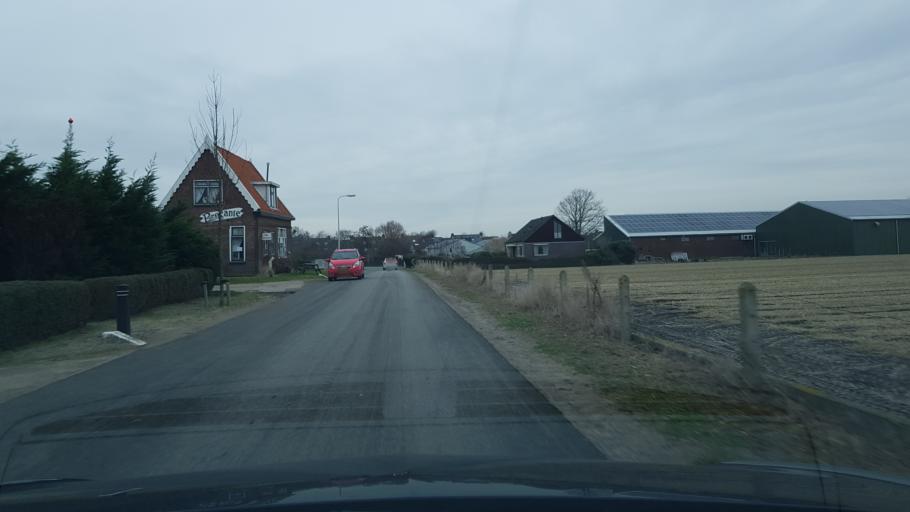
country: NL
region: South Holland
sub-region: Gemeente Noordwijkerhout
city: Noordwijkerhout
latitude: 52.2609
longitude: 4.4764
